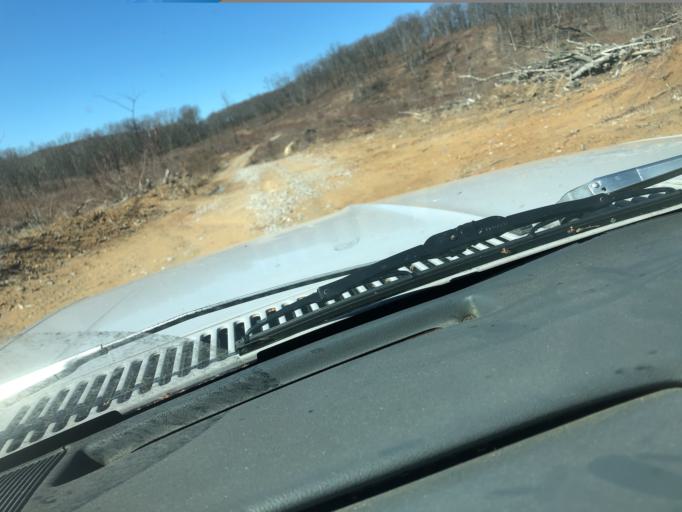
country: US
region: Tennessee
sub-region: Roane County
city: Rockwood
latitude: 35.9727
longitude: -84.7528
